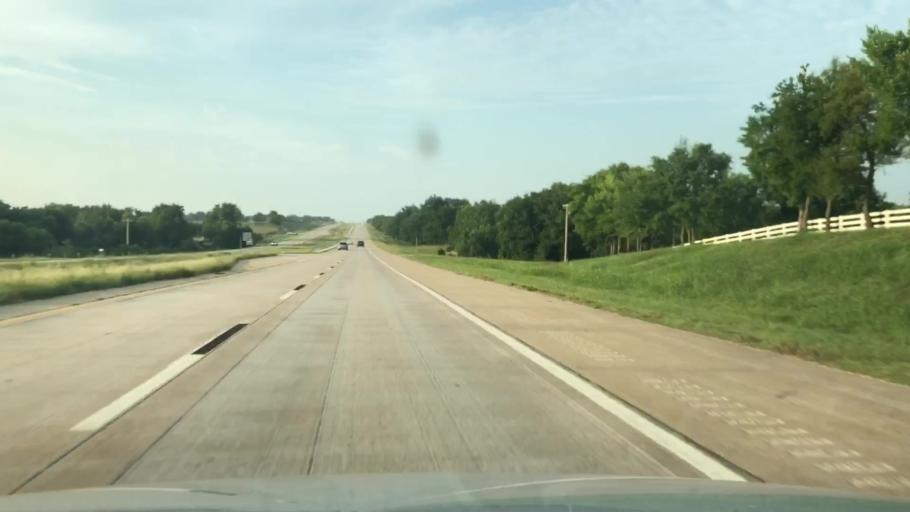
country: US
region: Oklahoma
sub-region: Osage County
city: Skiatook
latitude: 36.4428
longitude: -95.9208
